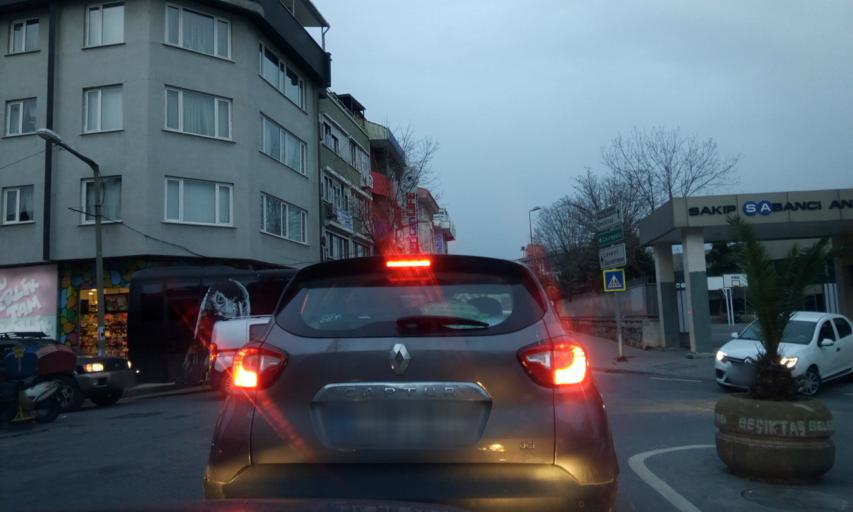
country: TR
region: Istanbul
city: Sisli
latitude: 41.0506
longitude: 29.0072
